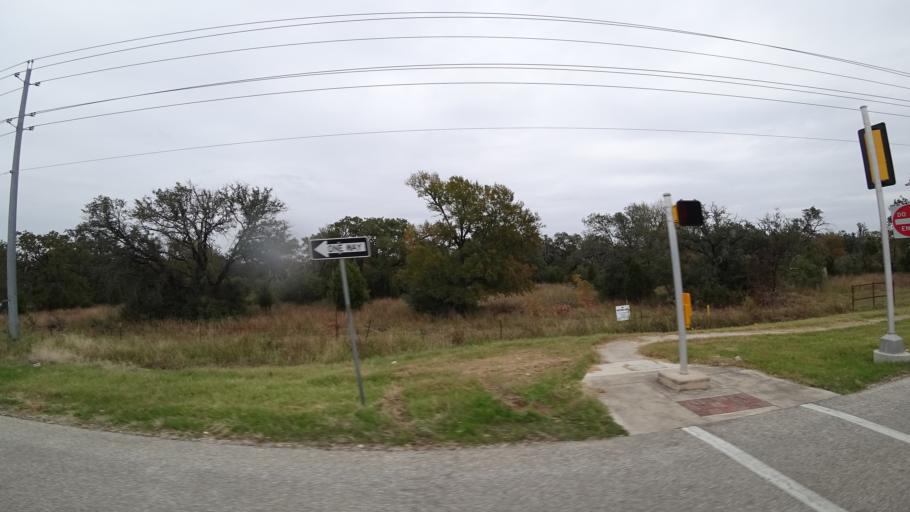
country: US
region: Texas
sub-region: Williamson County
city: Jollyville
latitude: 30.4502
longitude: -97.7471
